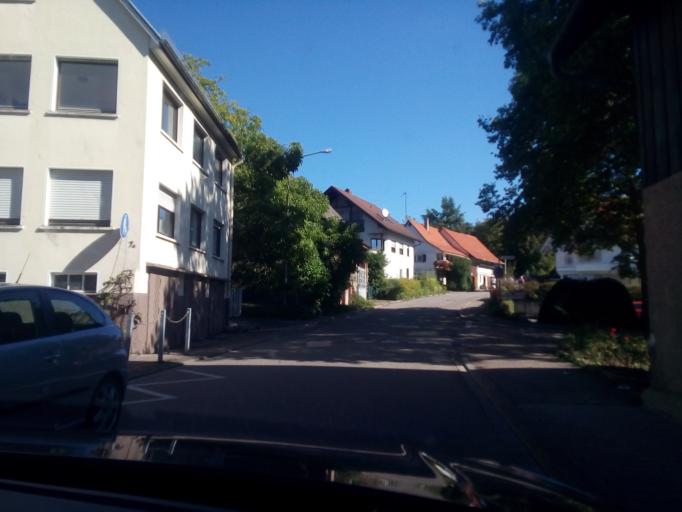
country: DE
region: Baden-Wuerttemberg
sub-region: Freiburg Region
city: Oberkirch
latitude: 48.5336
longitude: 8.0789
